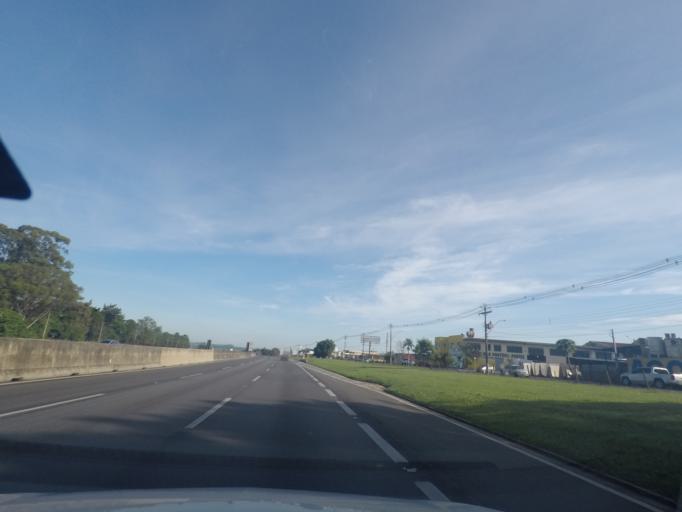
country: BR
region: Sao Paulo
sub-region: Americana
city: Americana
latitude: -22.7124
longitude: -47.2970
